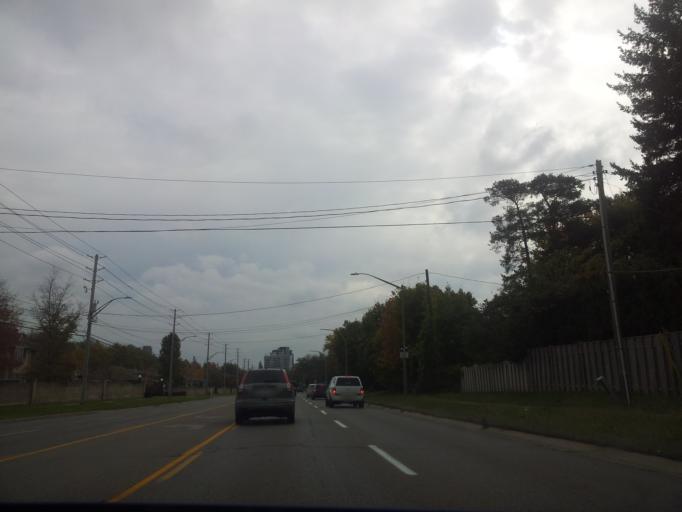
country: CA
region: Ontario
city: London
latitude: 43.0187
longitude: -81.2763
